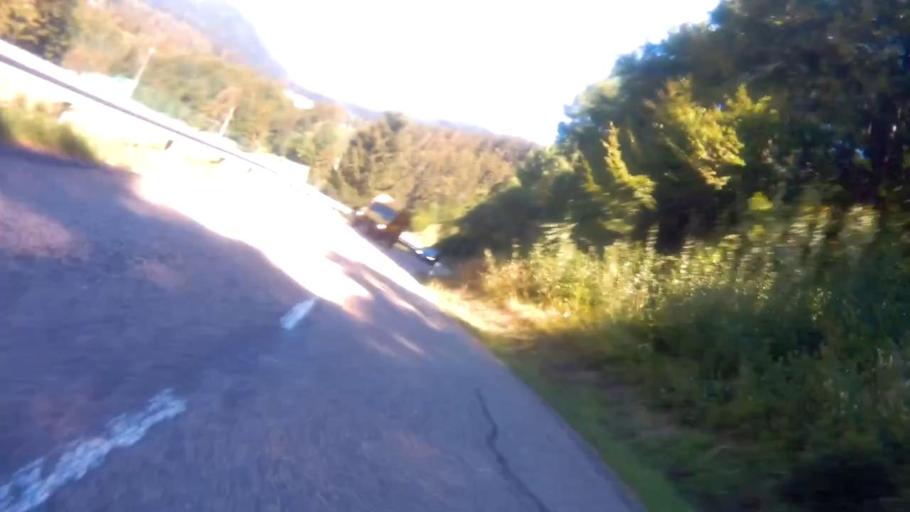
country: DE
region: Baden-Wuerttemberg
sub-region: Freiburg Region
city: Sulzburg
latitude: 47.7745
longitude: 7.7427
